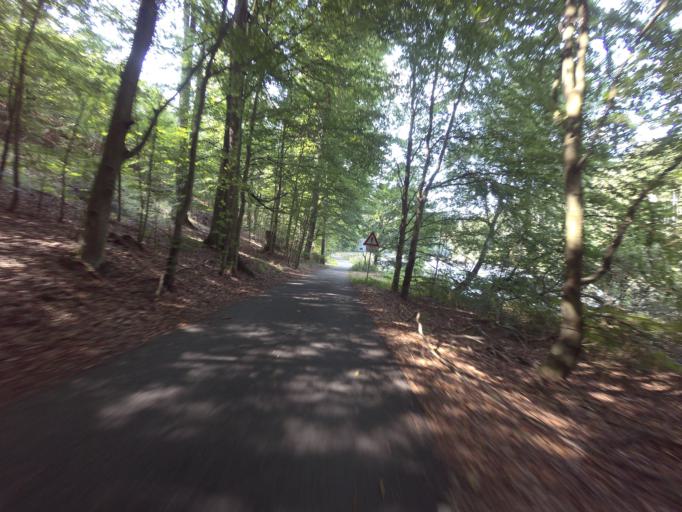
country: CZ
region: Jihocesky
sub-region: Okres Ceske Budejovice
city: Hluboka nad Vltavou
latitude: 49.0717
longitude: 14.4557
